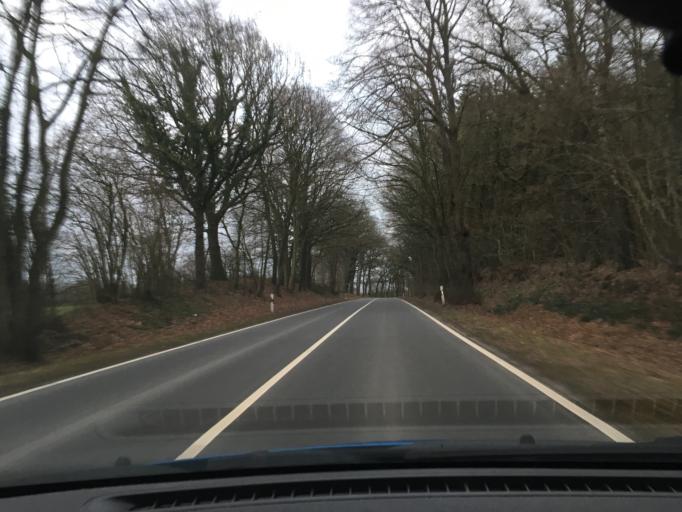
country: DE
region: Schleswig-Holstein
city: Kaaks
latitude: 53.9959
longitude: 9.4521
